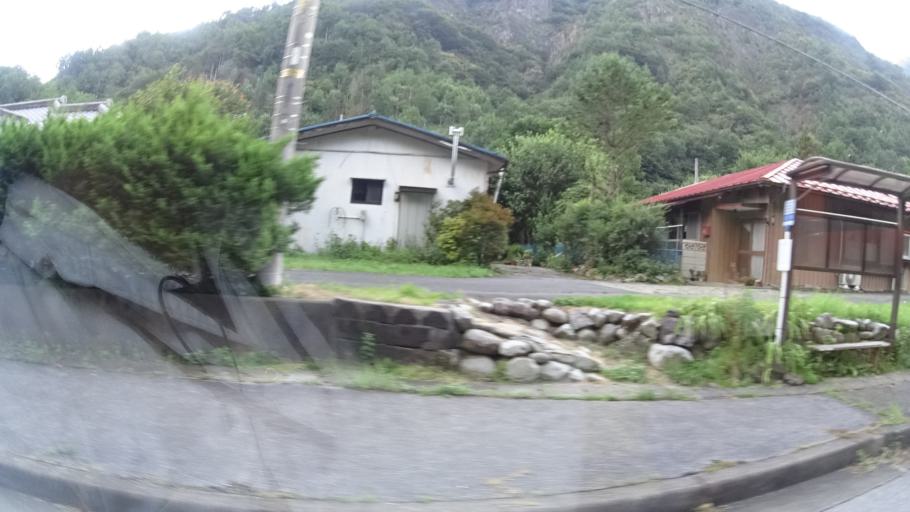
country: JP
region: Tochigi
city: Nikko
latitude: 36.6489
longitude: 139.4494
